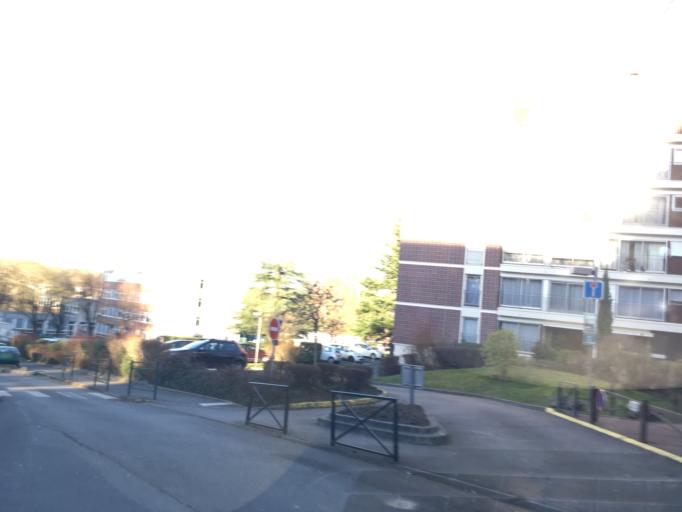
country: FR
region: Ile-de-France
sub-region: Departement de l'Essonne
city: Epinay-sous-Senart
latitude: 48.6924
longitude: 2.5096
